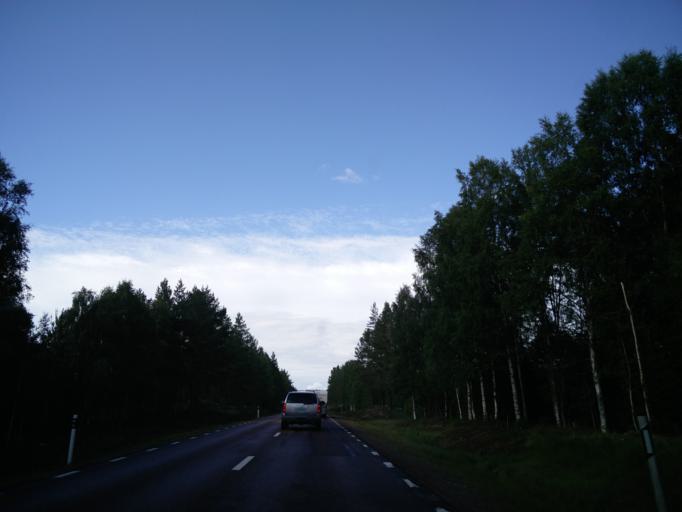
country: SE
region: Vaermland
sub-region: Hagfors Kommun
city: Ekshaerad
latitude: 60.4616
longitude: 13.2978
